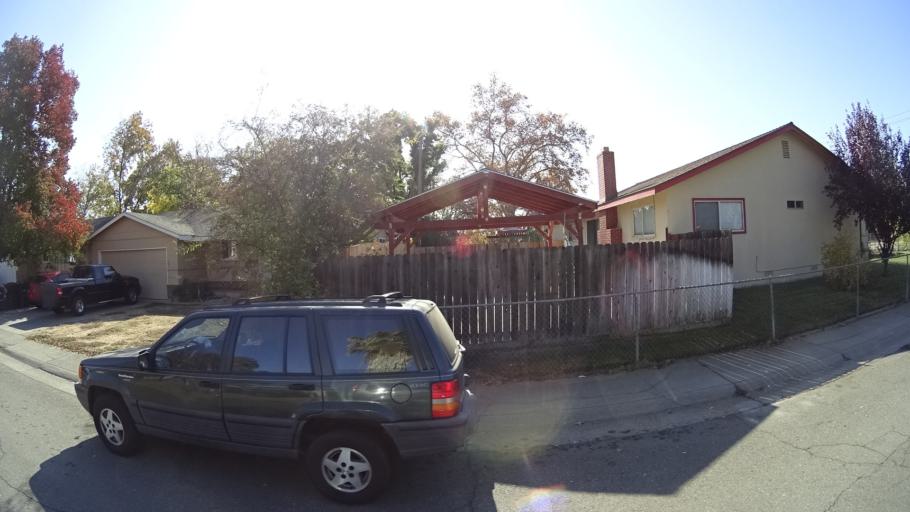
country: US
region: California
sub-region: Sacramento County
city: Citrus Heights
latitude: 38.6921
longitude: -121.2897
